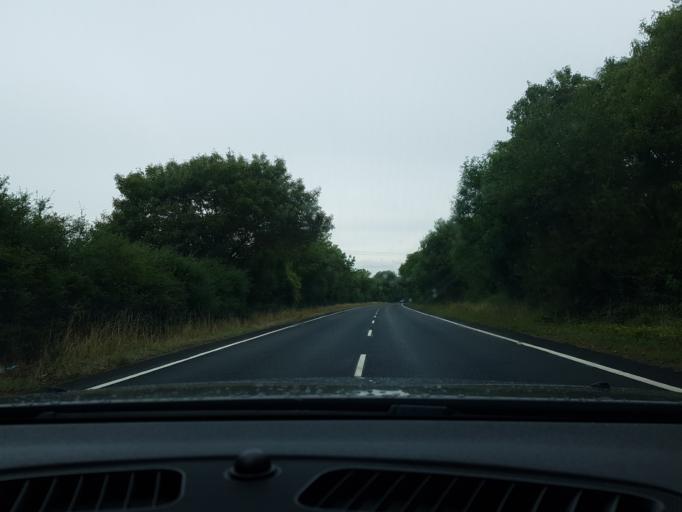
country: GB
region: England
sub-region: Hampshire
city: Odiham
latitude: 51.2640
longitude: -0.9450
